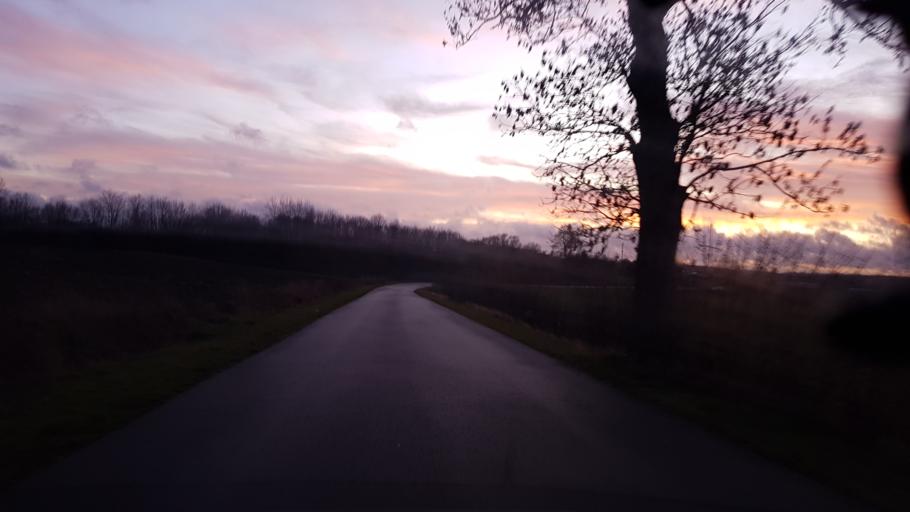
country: PL
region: Pomeranian Voivodeship
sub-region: Powiat bytowski
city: Tuchomie
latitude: 54.1278
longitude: 17.3499
